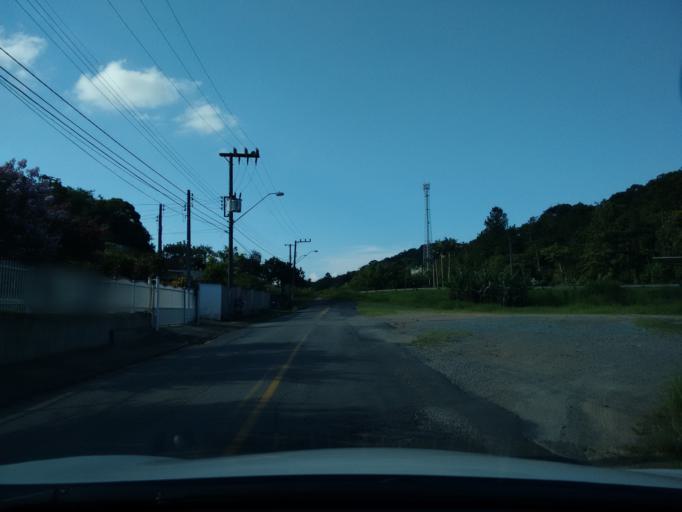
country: BR
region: Santa Catarina
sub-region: Blumenau
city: Blumenau
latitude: -26.8622
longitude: -49.0707
